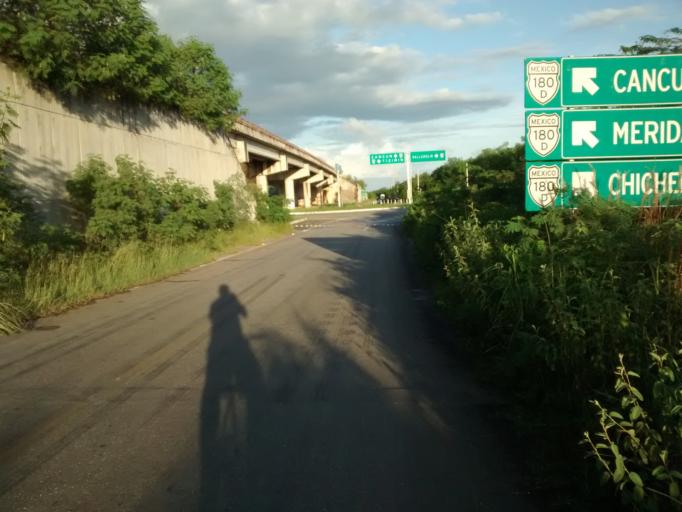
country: MX
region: Yucatan
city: Valladolid
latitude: 20.7250
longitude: -88.2038
